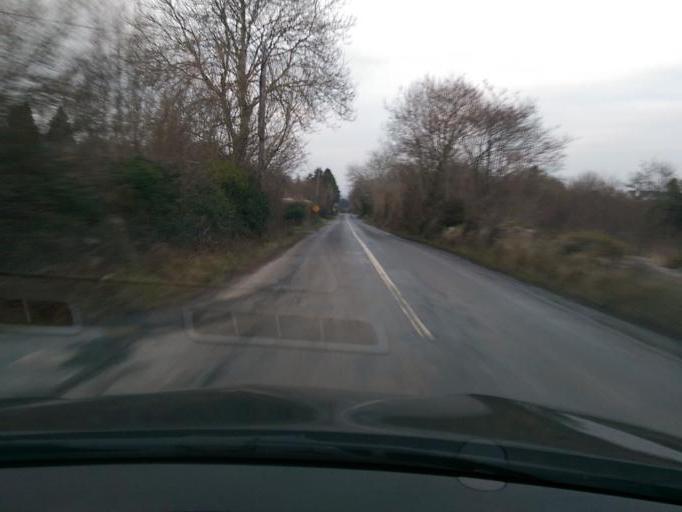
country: IE
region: Connaught
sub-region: County Galway
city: Moycullen
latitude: 53.3044
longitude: -9.1550
